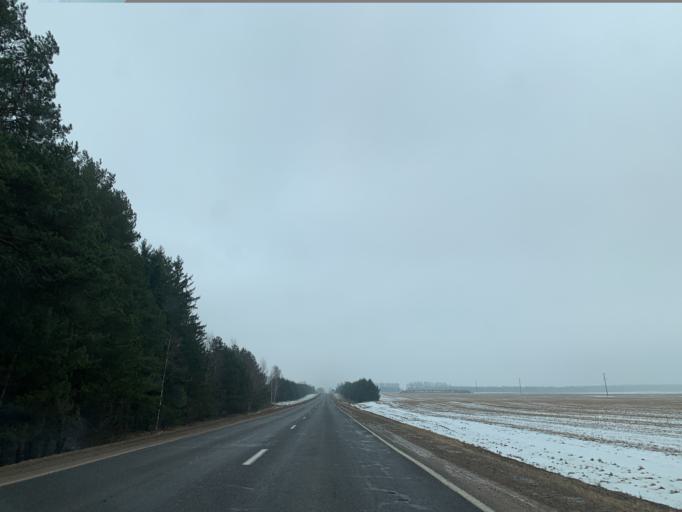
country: BY
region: Minsk
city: Haradzyeya
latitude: 53.3697
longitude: 26.5112
